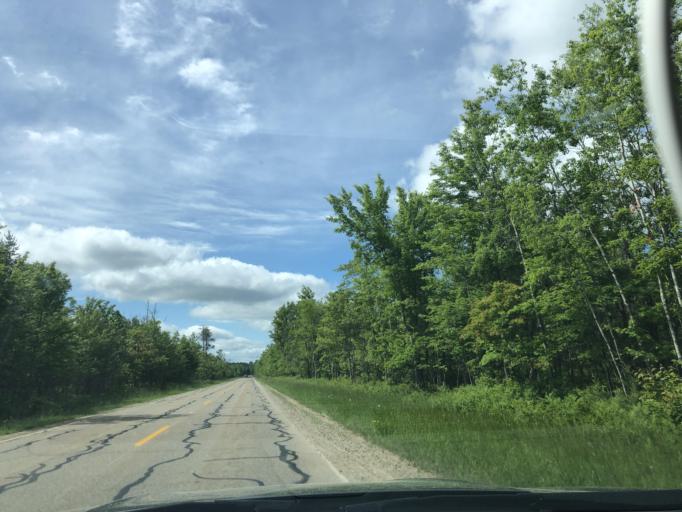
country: US
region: Michigan
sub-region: Roscommon County
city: Houghton Lake
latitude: 44.3448
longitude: -84.8546
